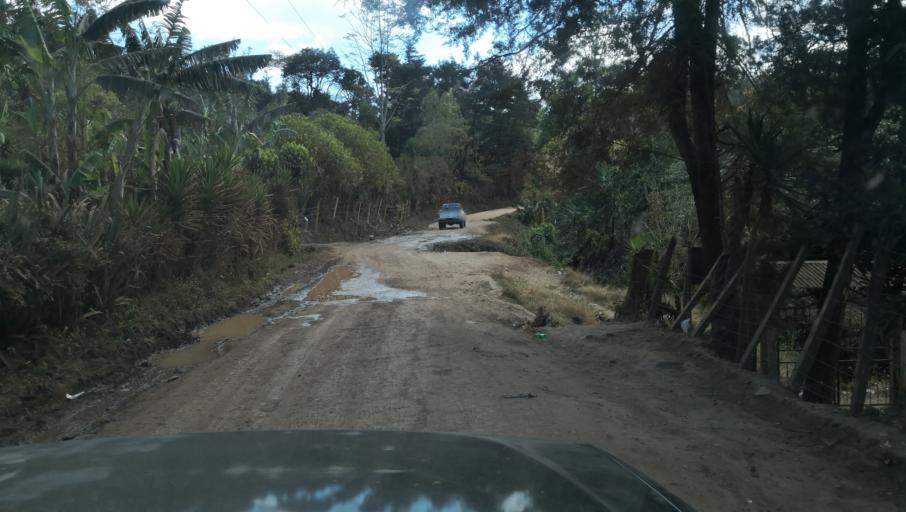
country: GT
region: Jalapa
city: San Carlos Alzatate
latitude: 14.3957
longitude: -89.9923
